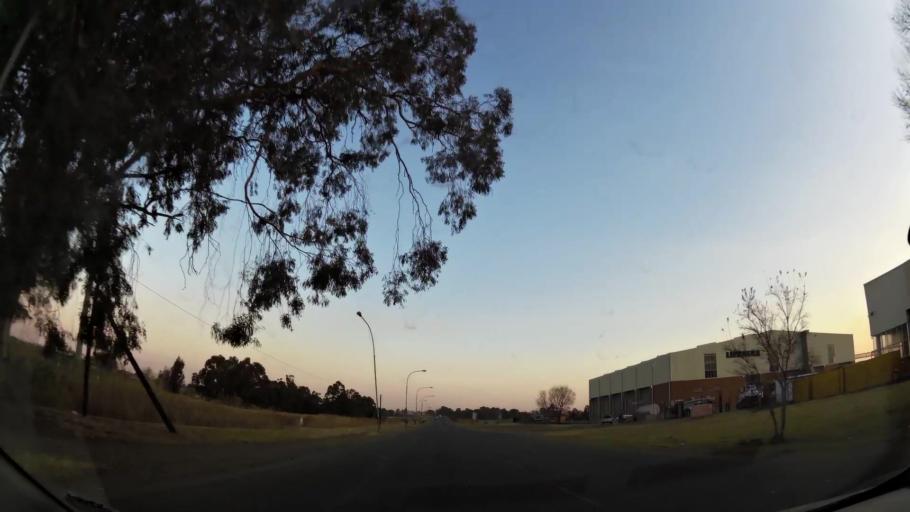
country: ZA
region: Gauteng
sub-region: Ekurhuleni Metropolitan Municipality
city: Springs
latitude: -26.2740
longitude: 28.4061
